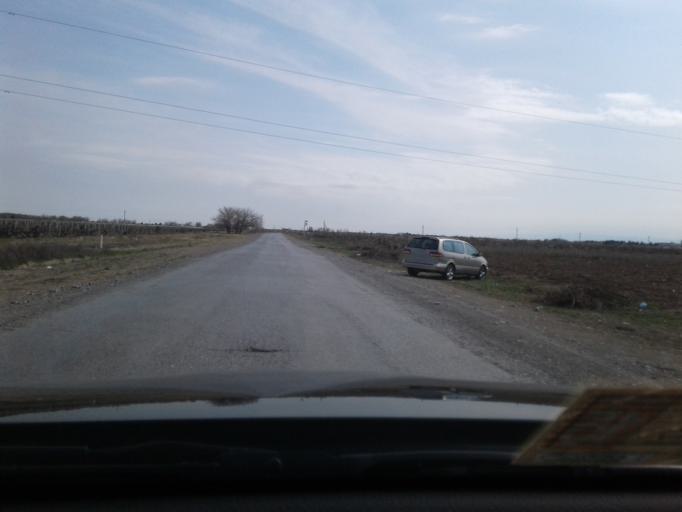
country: TM
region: Ahal
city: Ashgabat
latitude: 38.1174
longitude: 58.3570
